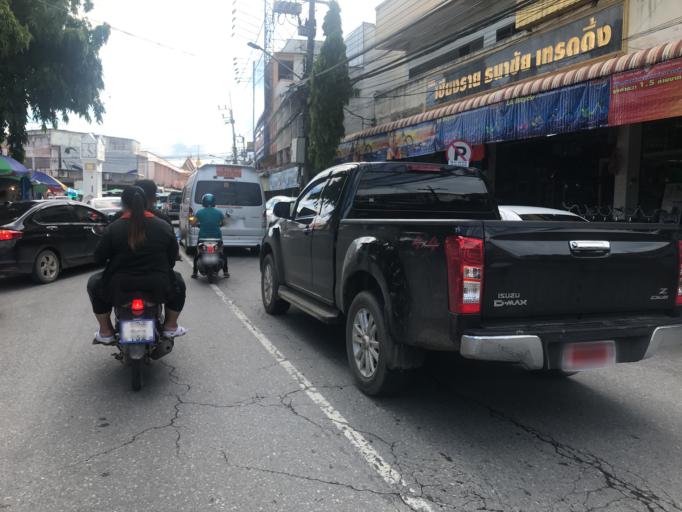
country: TH
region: Chiang Rai
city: Chiang Rai
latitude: 19.9105
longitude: 99.8310
